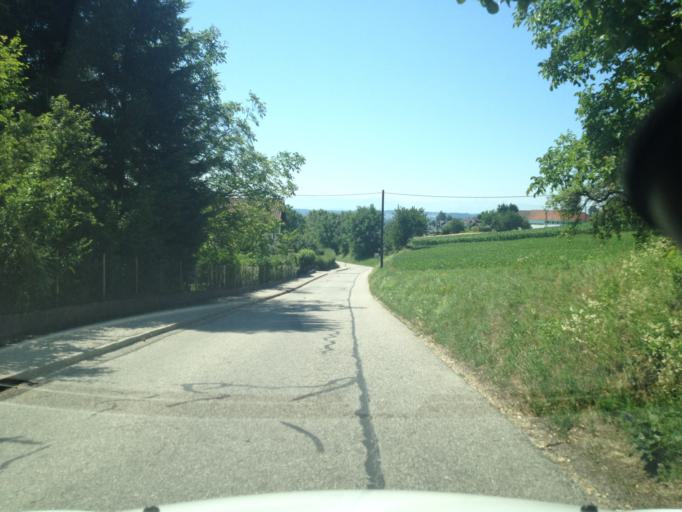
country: AT
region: Upper Austria
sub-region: Politischer Bezirk Linz-Land
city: Asten
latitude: 48.2674
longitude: 14.4276
